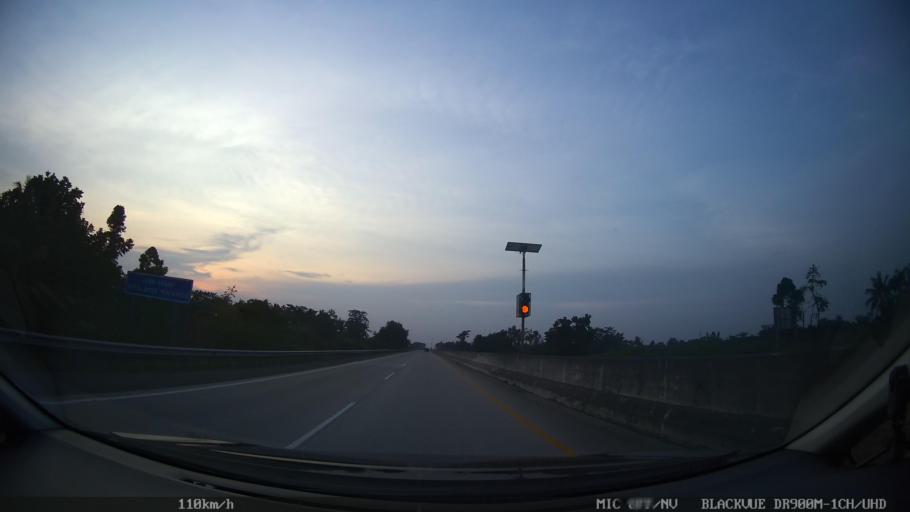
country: ID
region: Lampung
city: Pasuruan
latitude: -5.7456
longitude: 105.7002
